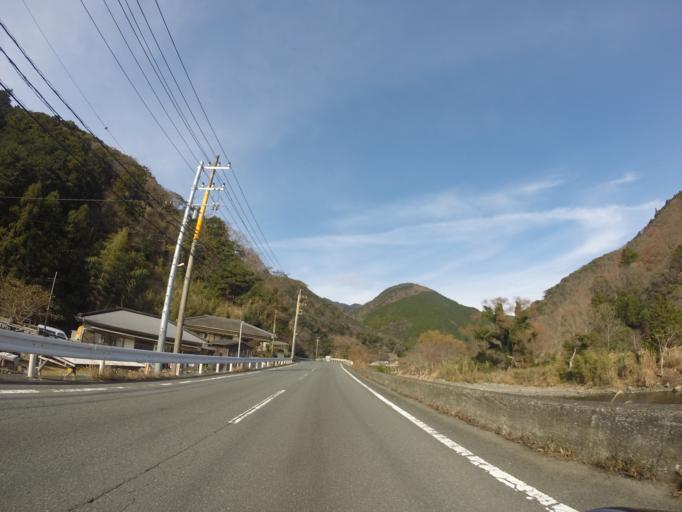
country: JP
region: Shizuoka
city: Heda
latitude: 34.7878
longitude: 138.8013
